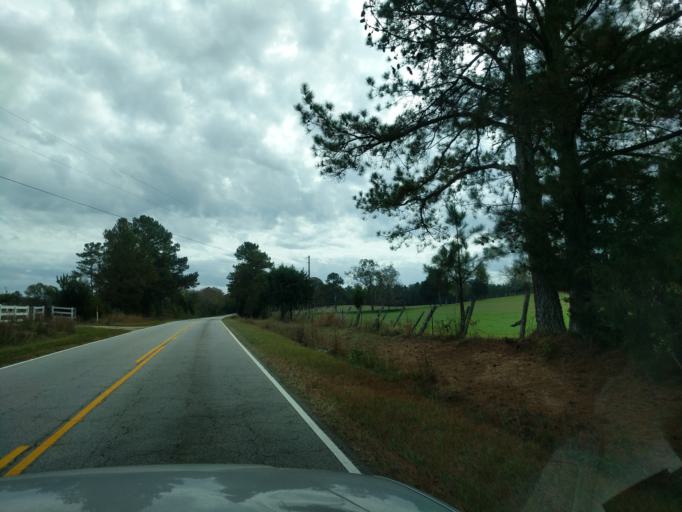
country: US
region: South Carolina
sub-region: Greenwood County
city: Ninety Six
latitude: 34.1652
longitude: -81.8564
